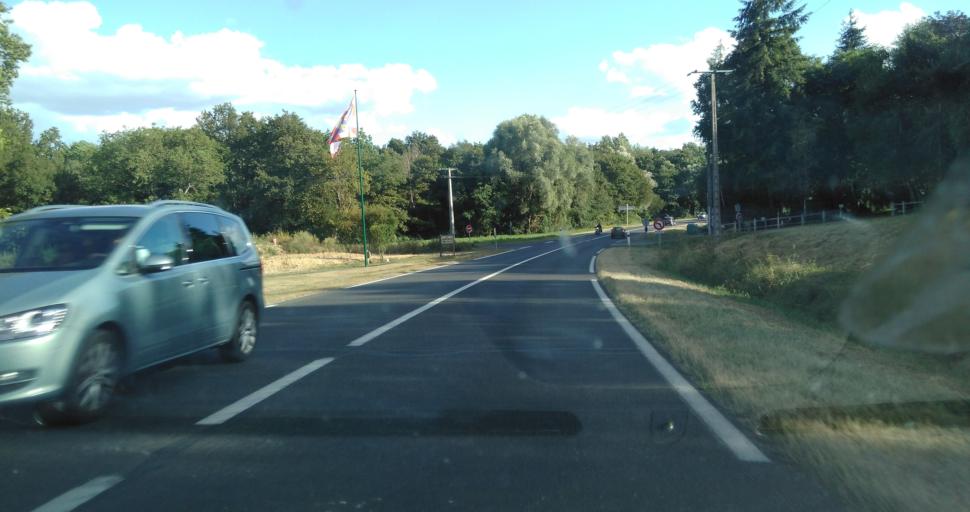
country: FR
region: Centre
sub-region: Departement d'Indre-et-Loire
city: Charge
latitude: 47.4078
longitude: 1.0207
